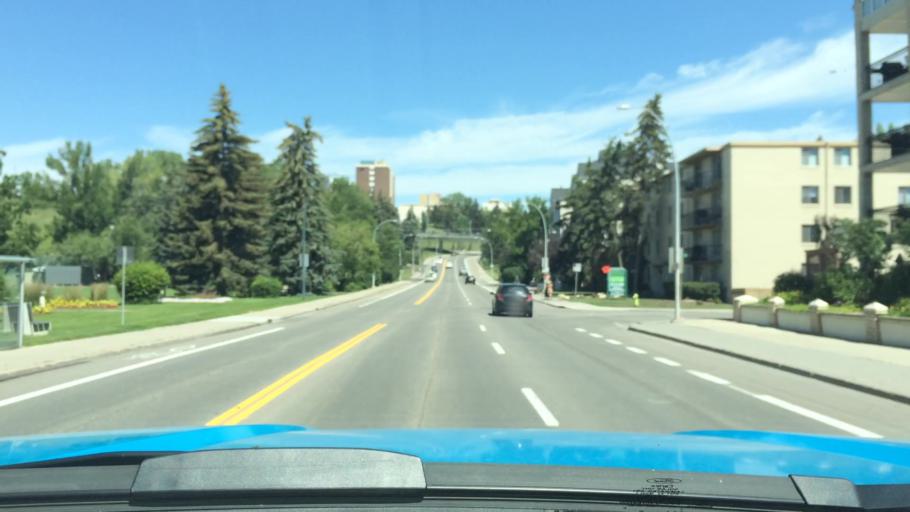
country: CA
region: Alberta
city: Calgary
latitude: 51.0580
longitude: -114.0860
